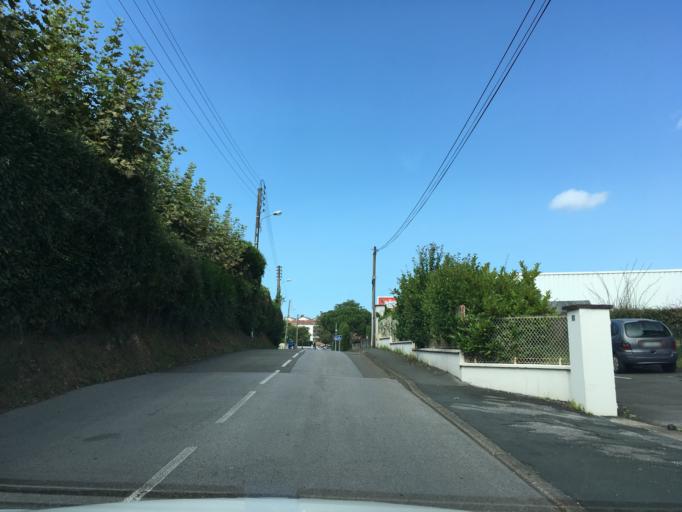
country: FR
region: Aquitaine
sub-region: Departement des Pyrenees-Atlantiques
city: Anglet
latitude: 43.4872
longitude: -1.5038
